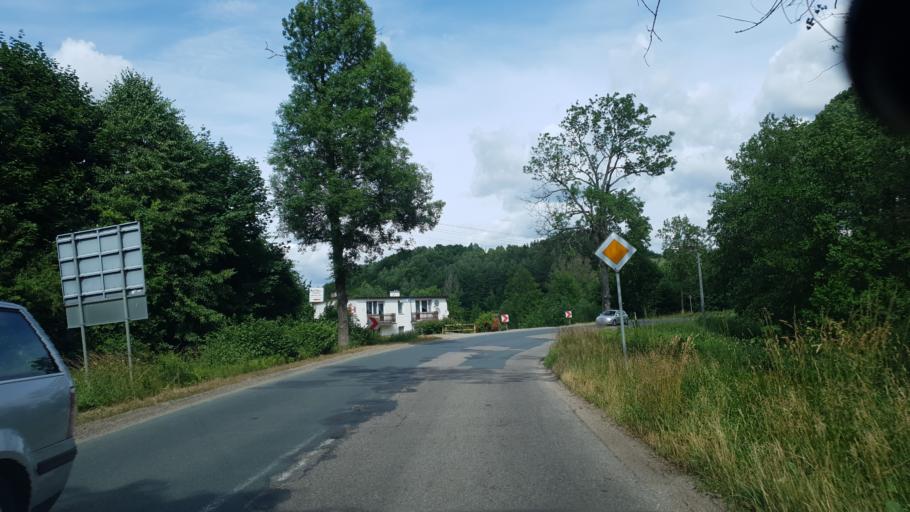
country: PL
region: Pomeranian Voivodeship
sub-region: Powiat kartuski
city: Chmielno
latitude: 54.2901
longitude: 18.1173
